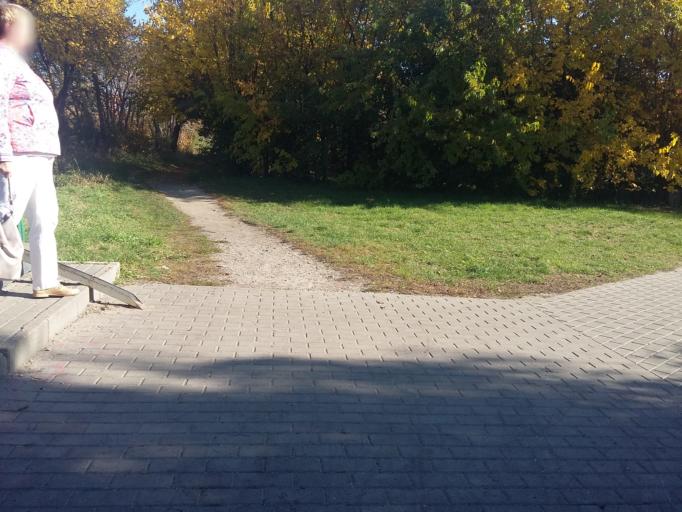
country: PL
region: Lodz Voivodeship
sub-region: Powiat pabianicki
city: Ksawerow
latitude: 51.7404
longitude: 19.4075
